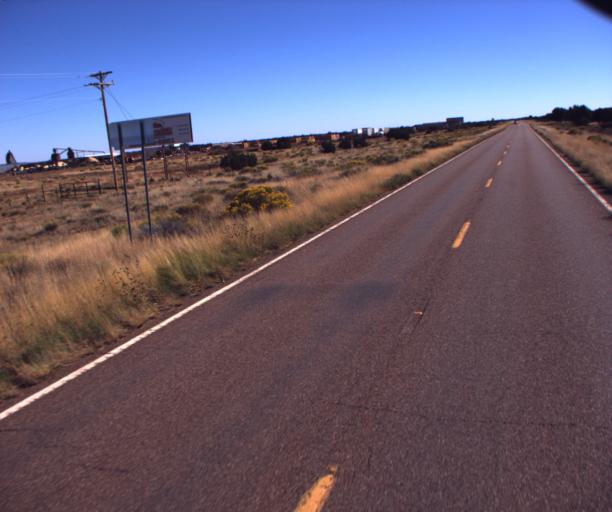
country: US
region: Arizona
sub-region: Navajo County
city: Heber-Overgaard
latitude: 34.4604
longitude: -110.4050
